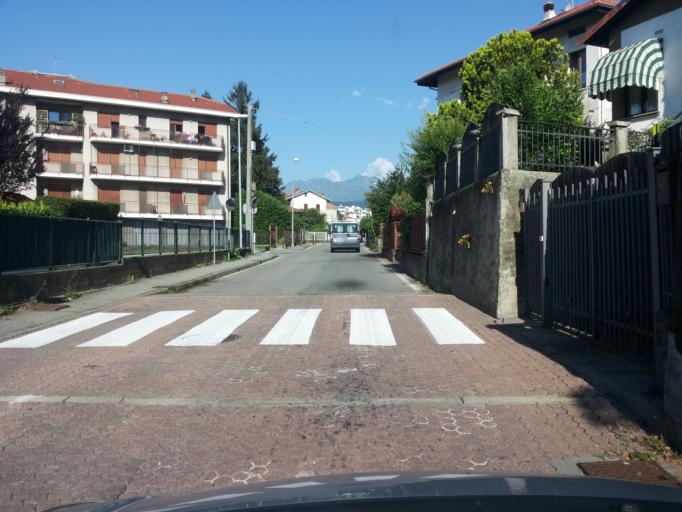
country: IT
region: Piedmont
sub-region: Provincia di Torino
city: Cascinette d'Ivrea
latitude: 45.4713
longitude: 7.8959
